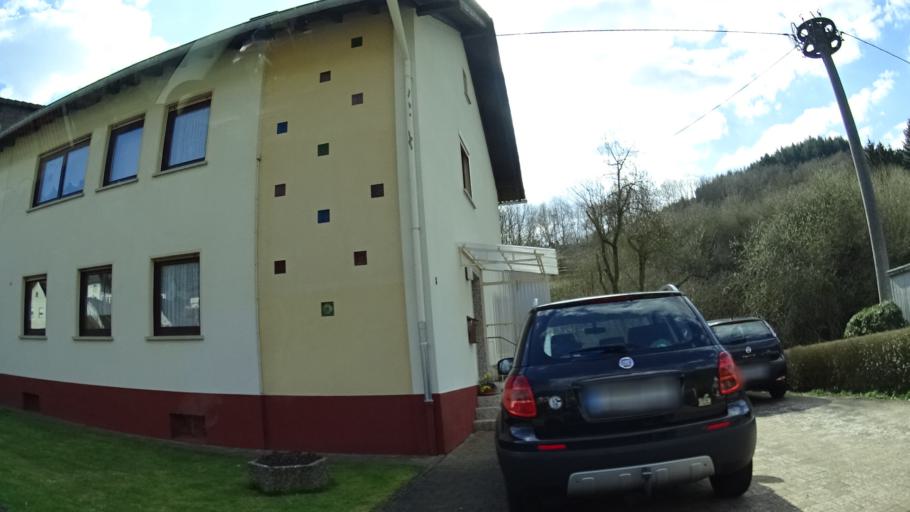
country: DE
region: Rheinland-Pfalz
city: Barenbach
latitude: 49.7495
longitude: 7.4390
